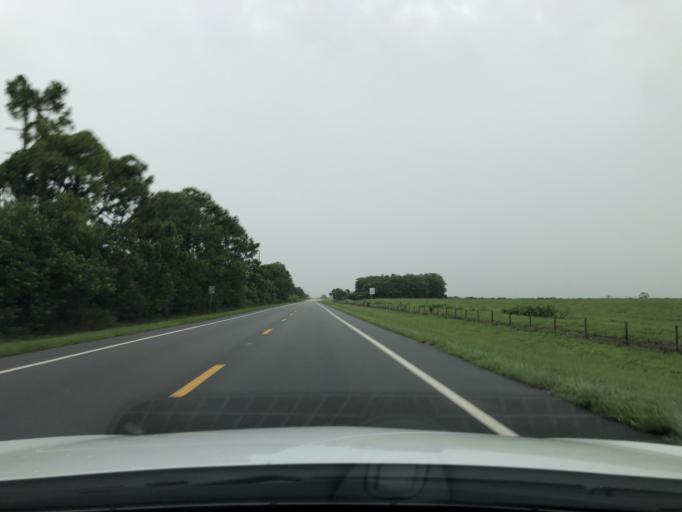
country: US
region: Florida
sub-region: Collier County
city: Immokalee
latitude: 26.2949
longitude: -81.4191
